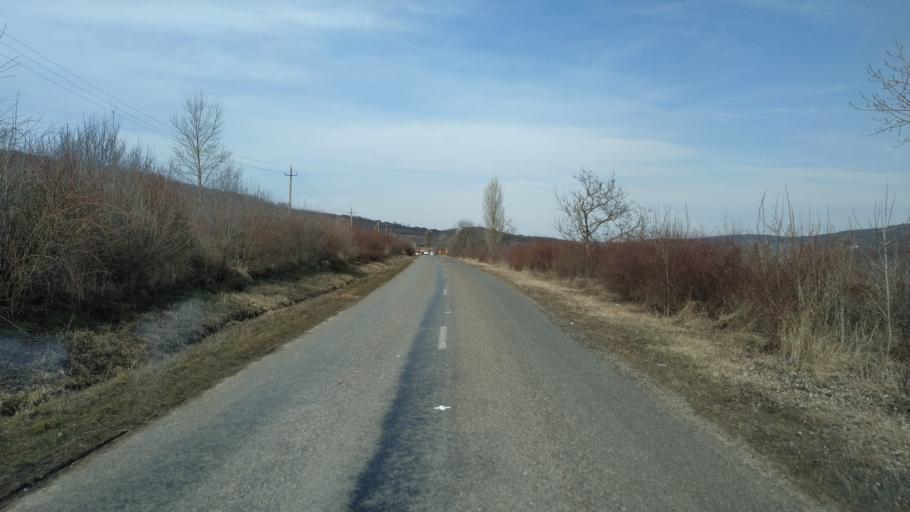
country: MD
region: Nisporeni
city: Nisporeni
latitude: 47.1809
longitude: 28.0789
